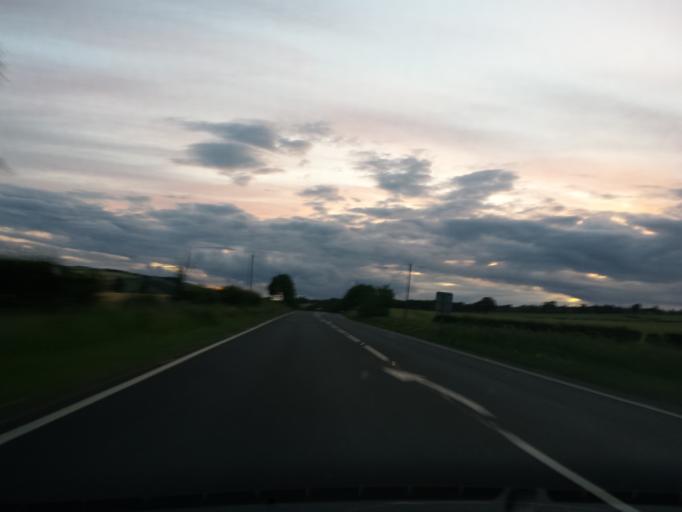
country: GB
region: Scotland
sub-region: The Scottish Borders
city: Chirnside
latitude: 55.8566
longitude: -2.2070
